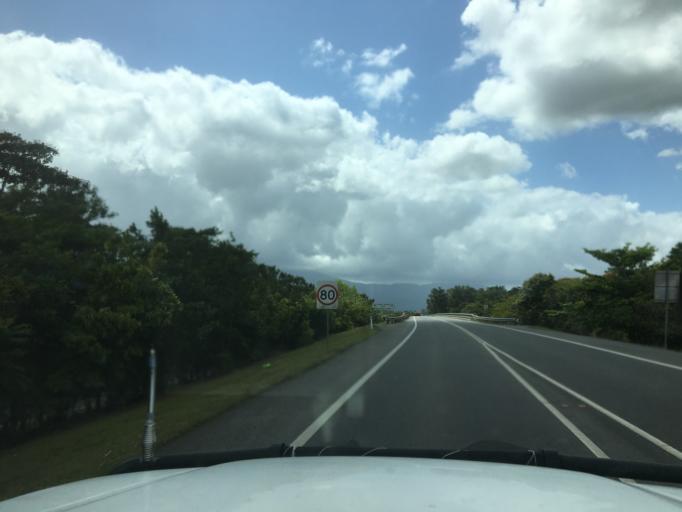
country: AU
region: Queensland
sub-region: Cairns
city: Woree
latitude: -17.1006
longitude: 145.7834
